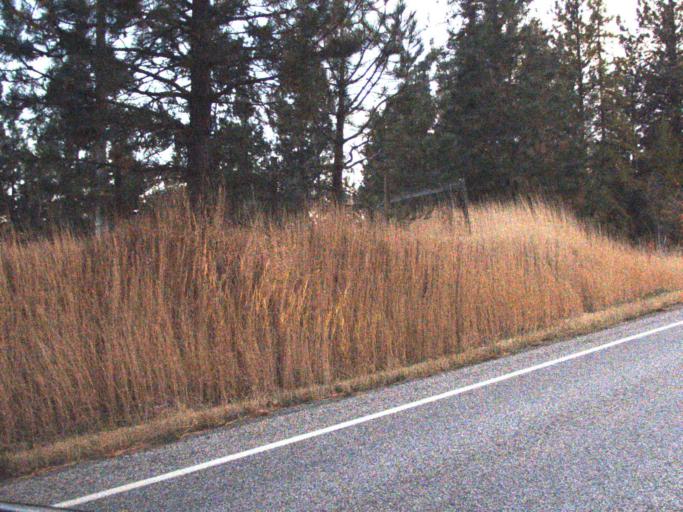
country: US
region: Washington
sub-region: Stevens County
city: Kettle Falls
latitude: 48.6206
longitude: -118.1326
